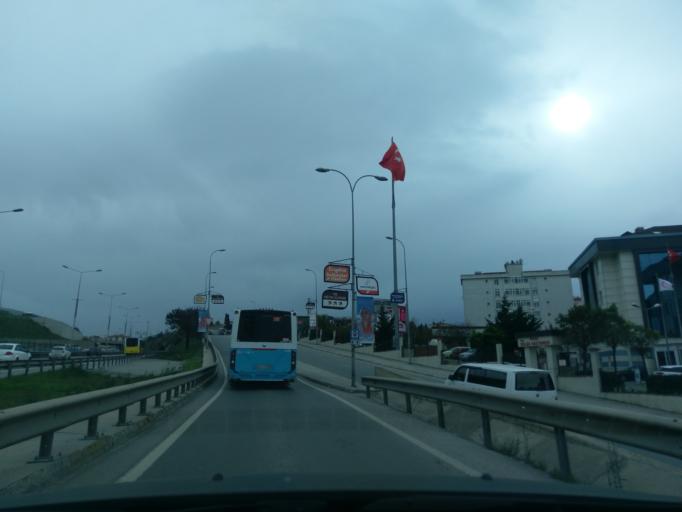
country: TR
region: Istanbul
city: Pendik
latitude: 40.8833
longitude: 29.2458
